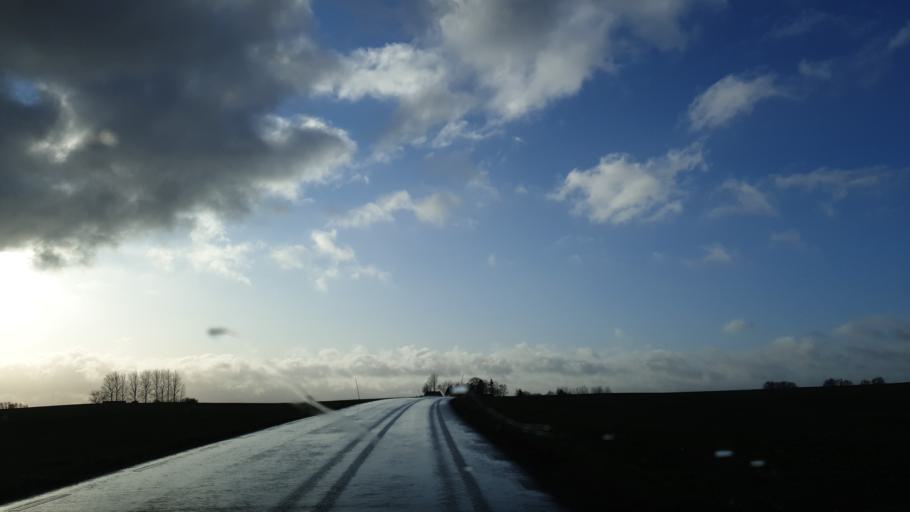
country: SE
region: Skane
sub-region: Skurups Kommun
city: Rydsgard
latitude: 55.4632
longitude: 13.5619
